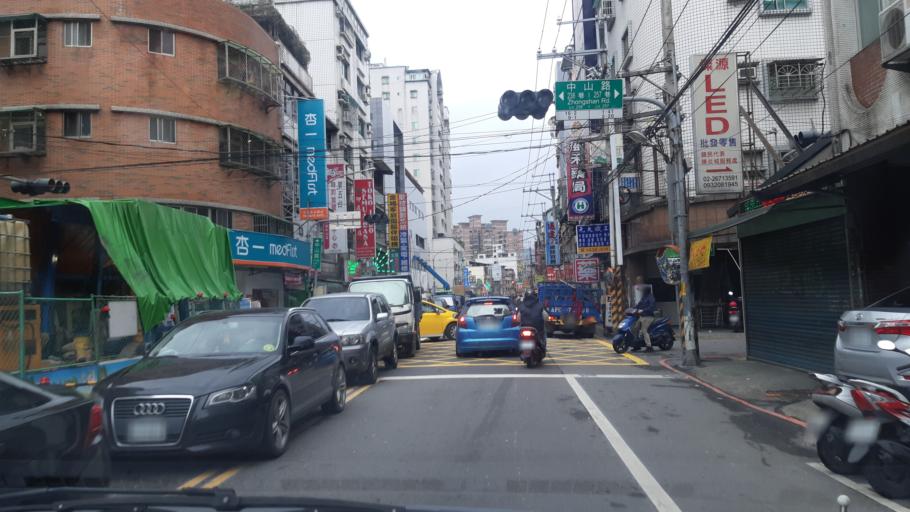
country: TW
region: Taiwan
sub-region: Taoyuan
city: Taoyuan
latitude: 24.9375
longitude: 121.3622
